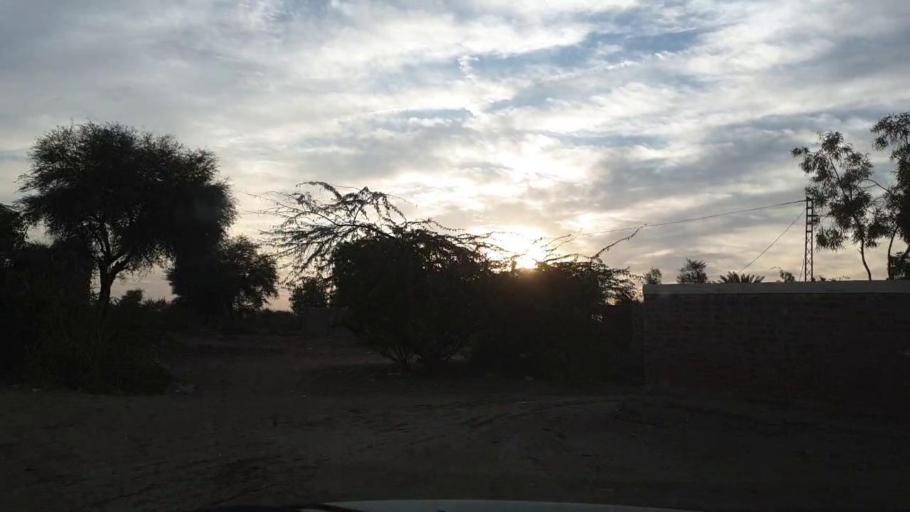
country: PK
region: Sindh
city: Pithoro
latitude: 25.6020
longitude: 69.2051
